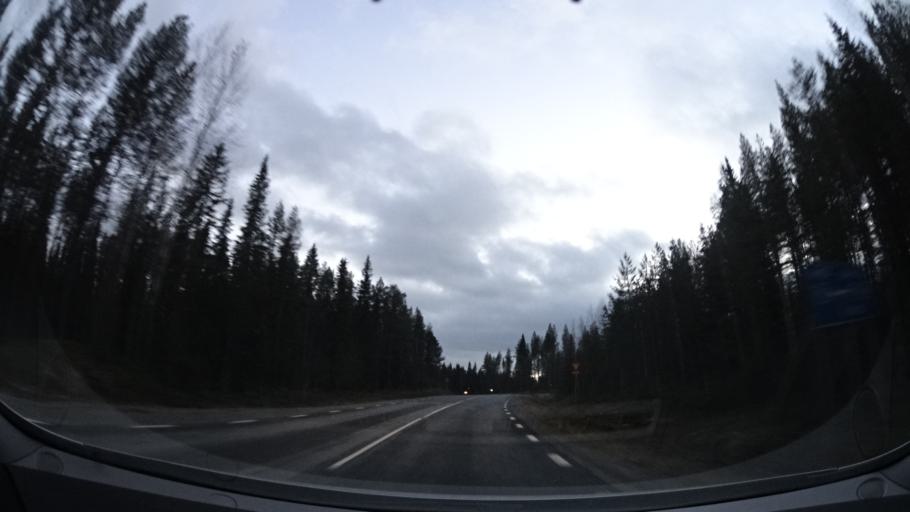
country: SE
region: Vaesterbotten
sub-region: Asele Kommun
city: Asele
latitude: 64.2022
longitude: 17.5115
